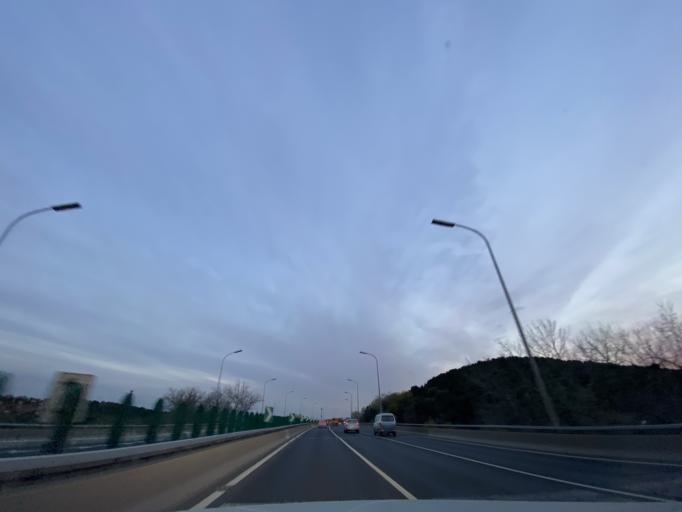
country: CN
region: Beijing
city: Haidian
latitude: 40.0067
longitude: 116.2650
